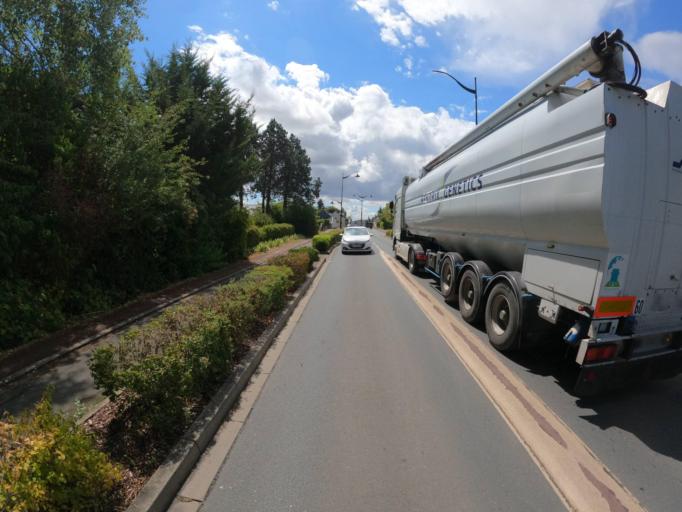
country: FR
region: Pays de la Loire
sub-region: Departement de Maine-et-Loire
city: Feneu
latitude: 47.5749
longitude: -0.5930
